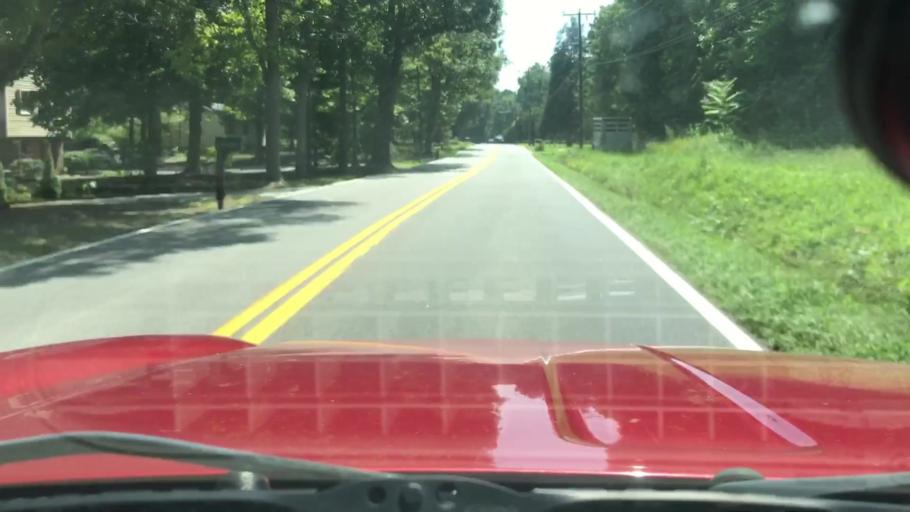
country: US
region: Virginia
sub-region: City of Colonial Heights
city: Colonial Heights
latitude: 37.3131
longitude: -77.4132
